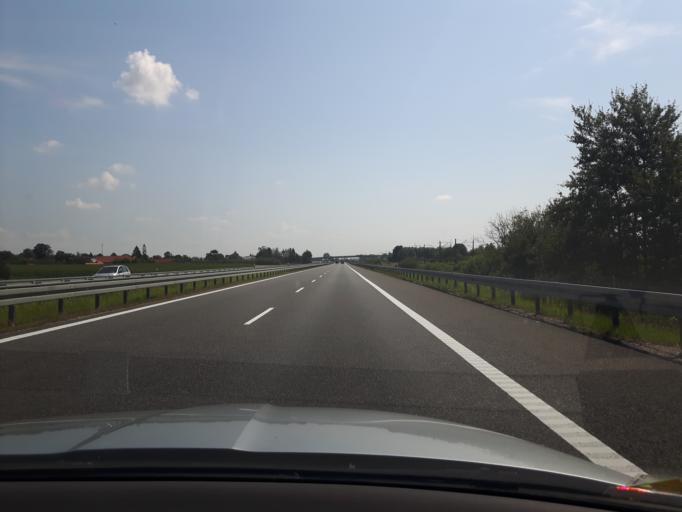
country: PL
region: Warmian-Masurian Voivodeship
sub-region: Powiat elblaski
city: Gronowo Gorne
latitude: 54.1067
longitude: 19.5027
